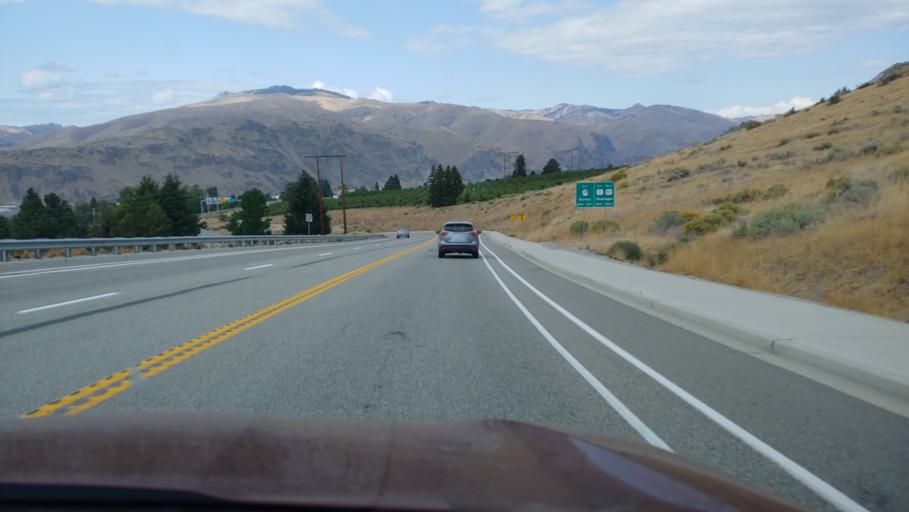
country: US
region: Washington
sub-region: Chelan County
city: Sunnyslope
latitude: 47.4658
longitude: -120.2962
